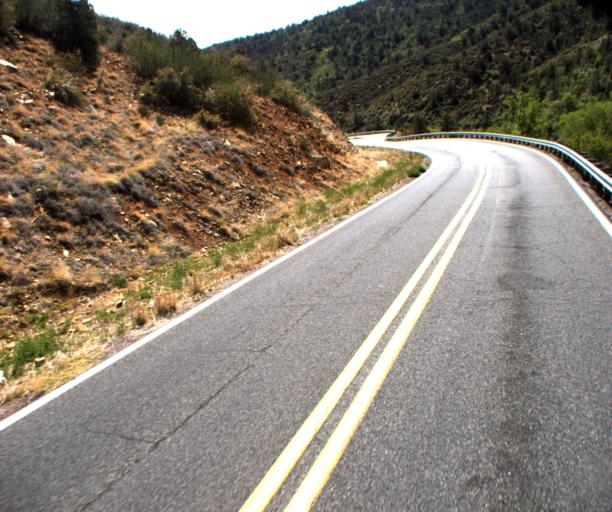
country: US
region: Arizona
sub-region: Yavapai County
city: Clarkdale
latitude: 34.7395
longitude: -112.1321
